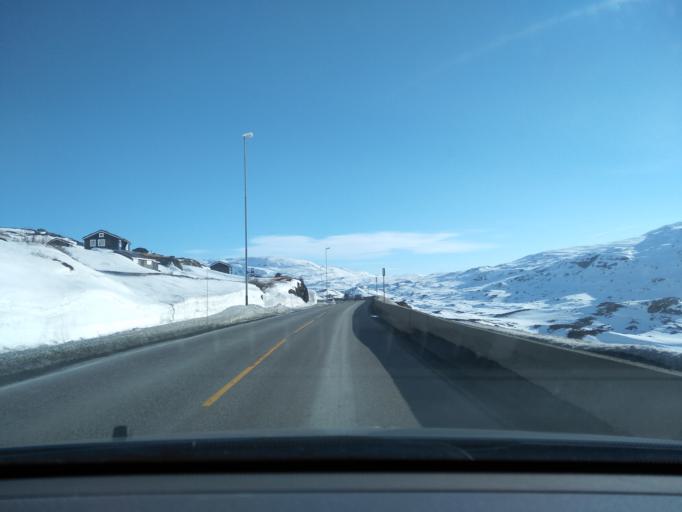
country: NO
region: Hordaland
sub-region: Odda
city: Odda
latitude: 59.8472
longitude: 6.9686
